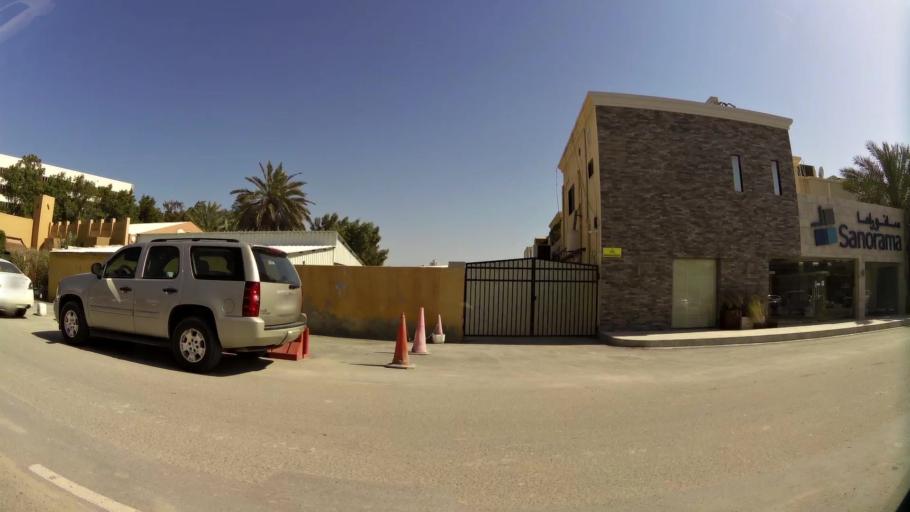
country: BH
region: Manama
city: Manama
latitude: 26.2154
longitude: 50.5699
